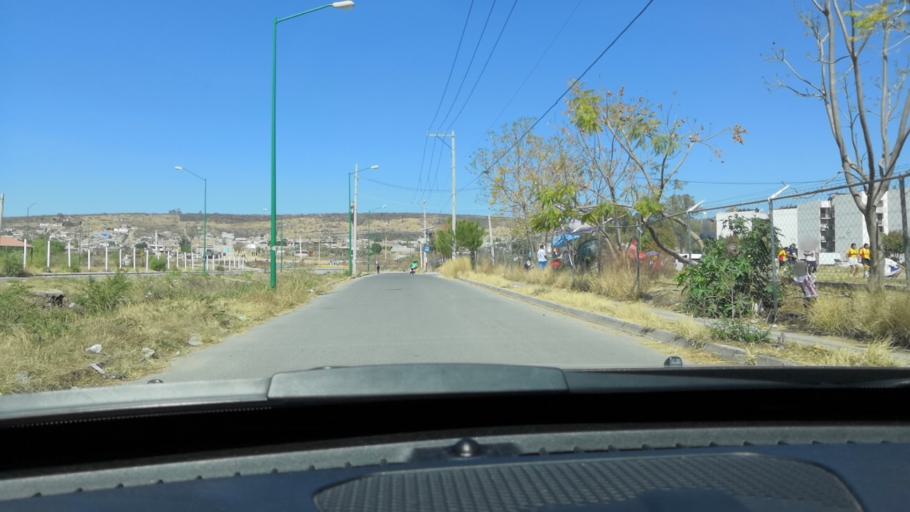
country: MX
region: Guanajuato
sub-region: Leon
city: Rizos de la Joya (Rizos del Saucillo)
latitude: 21.1459
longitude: -101.7531
